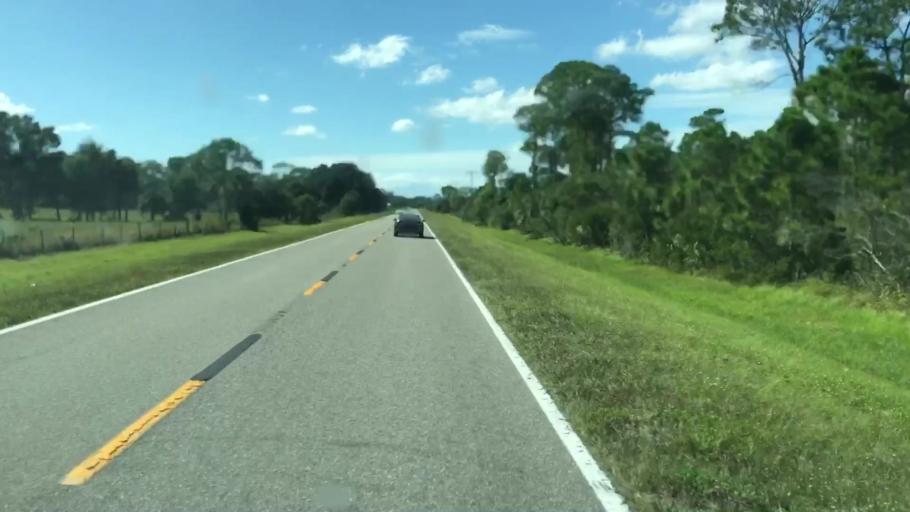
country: US
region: Florida
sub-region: Lee County
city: Fort Myers Shores
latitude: 26.7401
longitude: -81.7508
